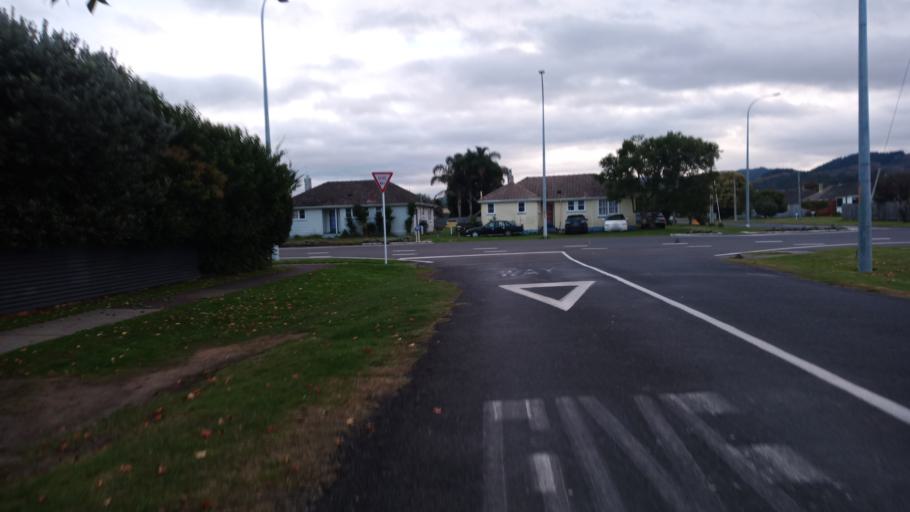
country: NZ
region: Gisborne
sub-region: Gisborne District
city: Gisborne
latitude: -38.6538
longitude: 178.0024
